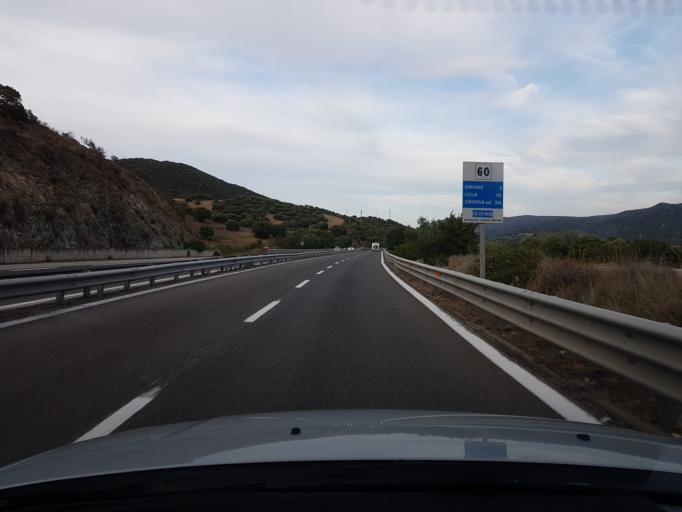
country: IT
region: Sardinia
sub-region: Provincia di Nuoro
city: Orune
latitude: 40.3680
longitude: 9.3733
